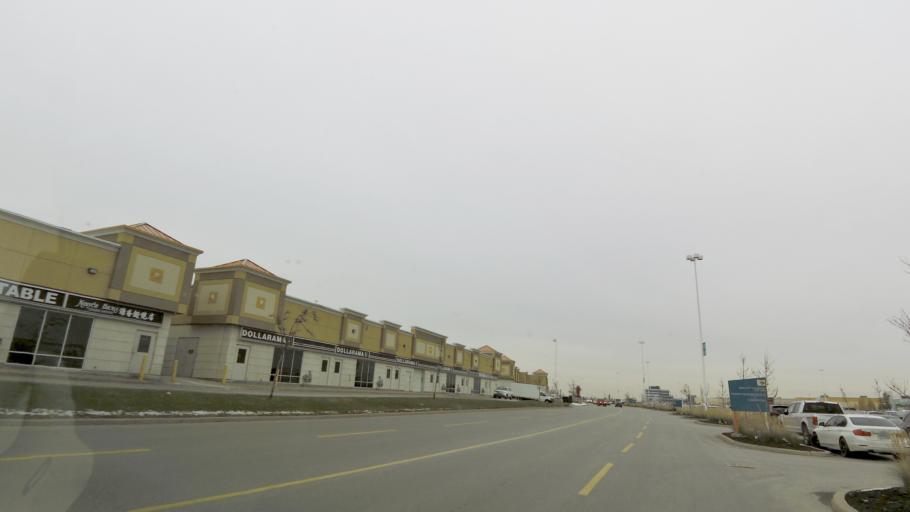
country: CA
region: Ontario
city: Vaughan
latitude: 43.8270
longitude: -79.5424
